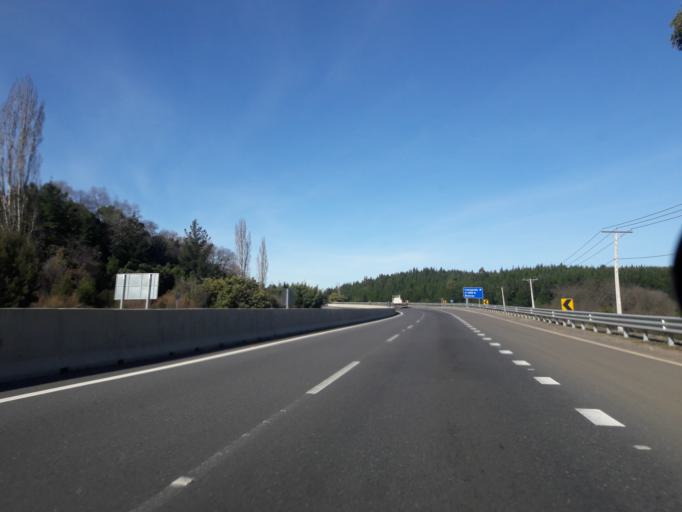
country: CL
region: Biobio
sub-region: Provincia de Biobio
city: Yumbel
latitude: -36.9558
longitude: -72.7448
